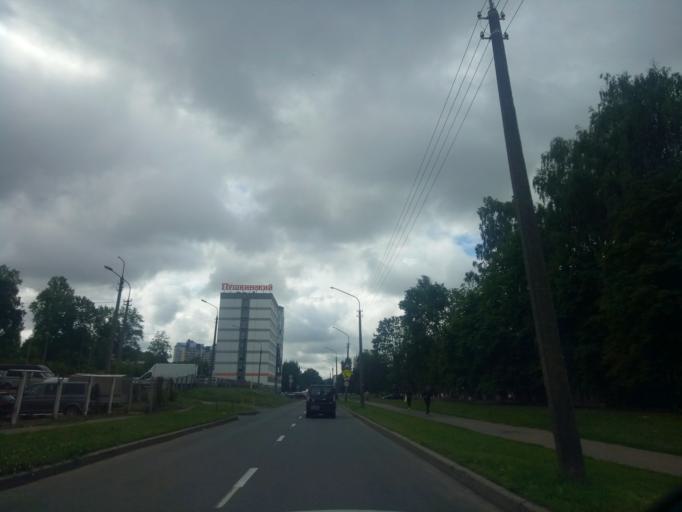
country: BY
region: Minsk
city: Novoye Medvezhino
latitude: 53.9068
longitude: 27.5013
